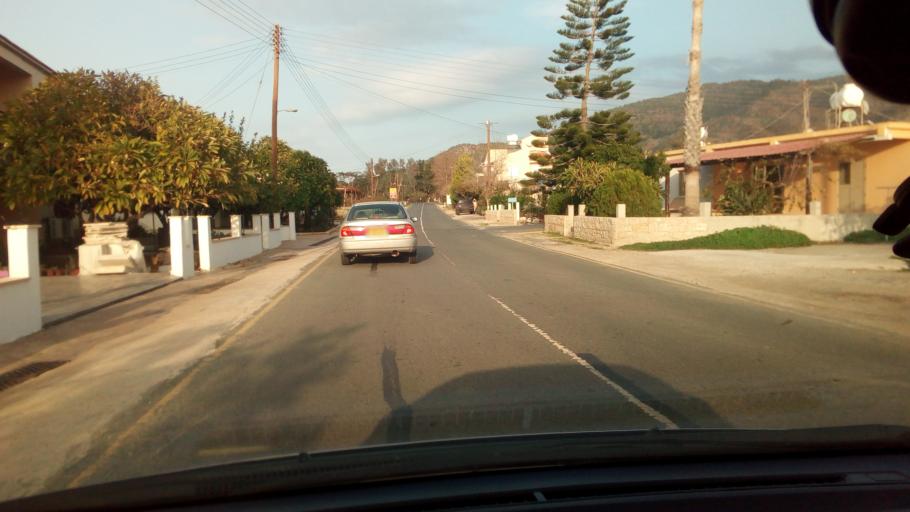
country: CY
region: Pafos
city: Polis
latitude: 35.1222
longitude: 32.5146
